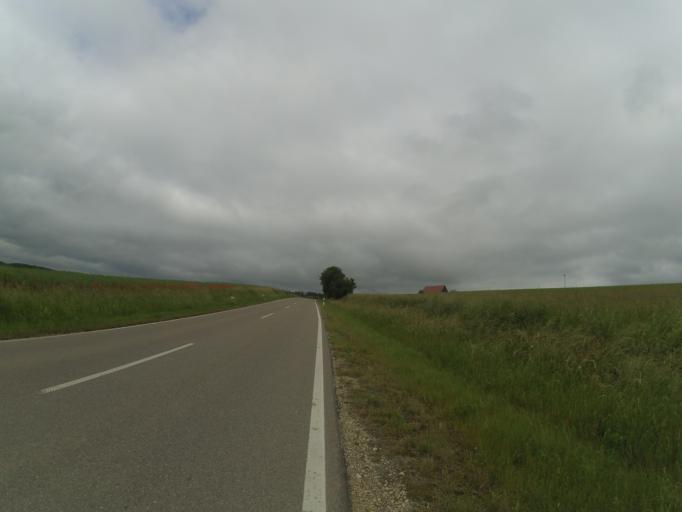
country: DE
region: Baden-Wuerttemberg
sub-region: Tuebingen Region
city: Bernstadt
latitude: 48.4841
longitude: 10.0375
